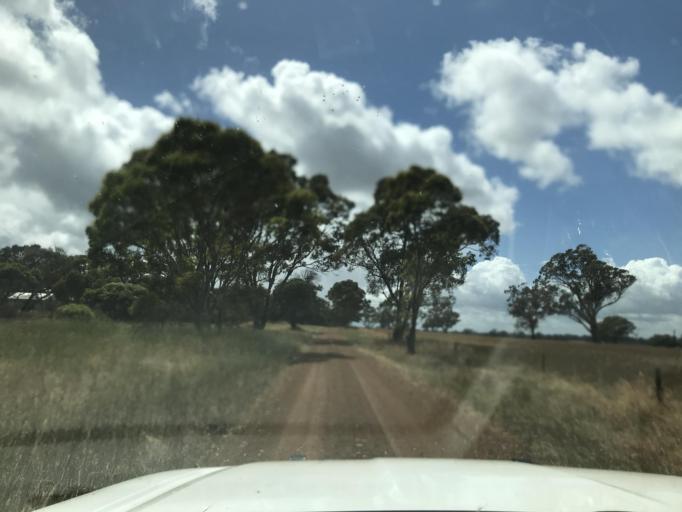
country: AU
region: South Australia
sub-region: Wattle Range
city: Penola
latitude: -37.1825
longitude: 141.4531
